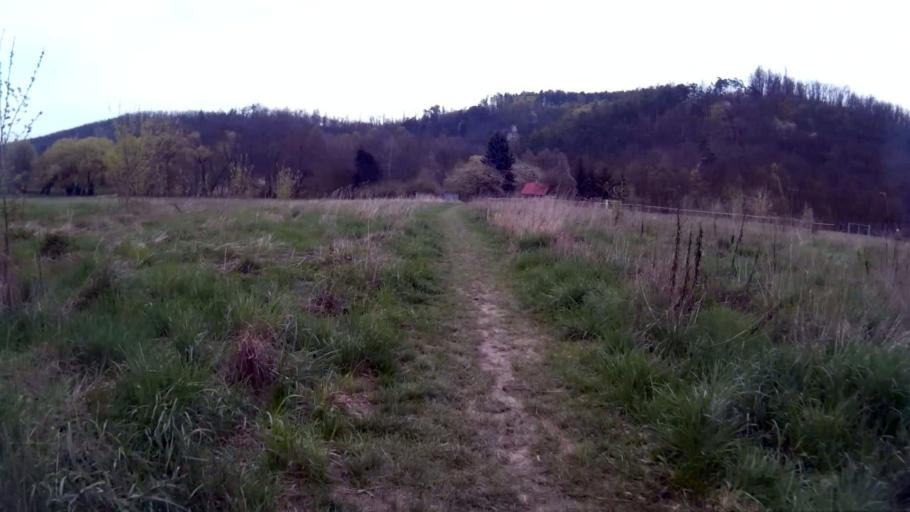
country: CZ
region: South Moravian
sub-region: Mesto Brno
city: Mokra Hora
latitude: 49.2260
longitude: 16.5608
